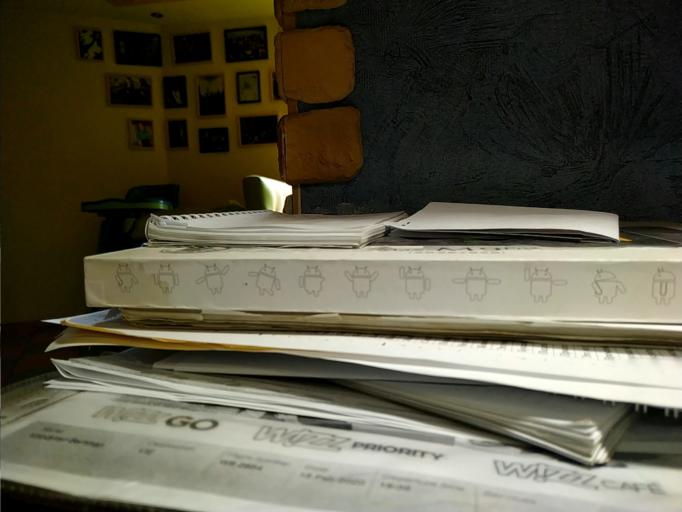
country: RU
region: Pskov
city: Plyussa
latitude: 58.3859
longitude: 29.7128
